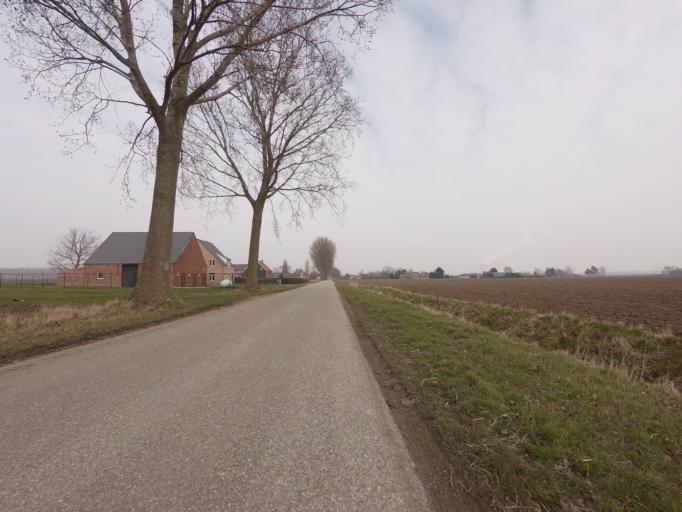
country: BE
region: Flanders
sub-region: Provincie Oost-Vlaanderen
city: Beveren
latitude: 51.3223
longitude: 4.1992
